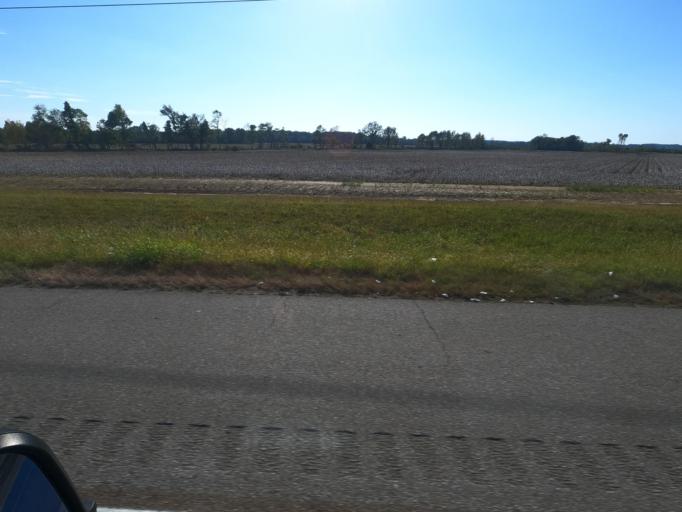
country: US
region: Tennessee
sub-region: Crockett County
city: Alamo
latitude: 35.8569
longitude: -89.2021
